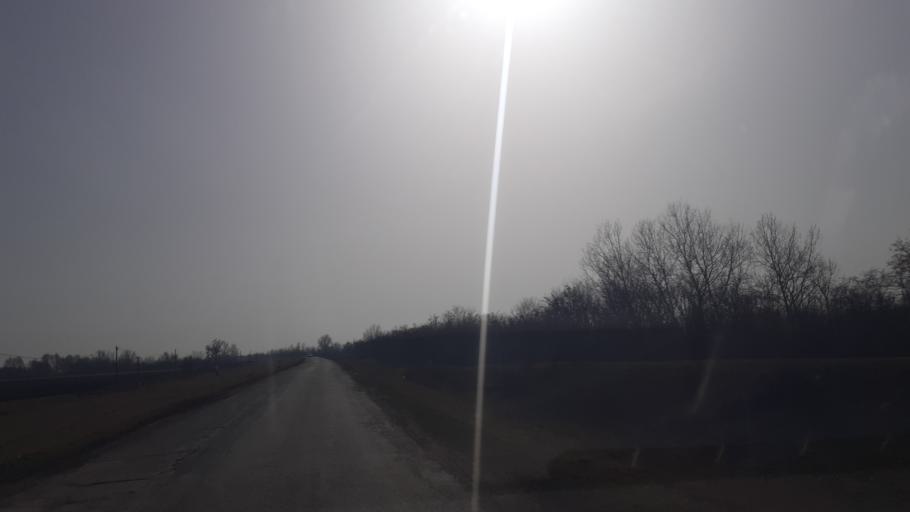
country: HU
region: Fejer
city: Racalmas
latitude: 47.0285
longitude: 18.9838
